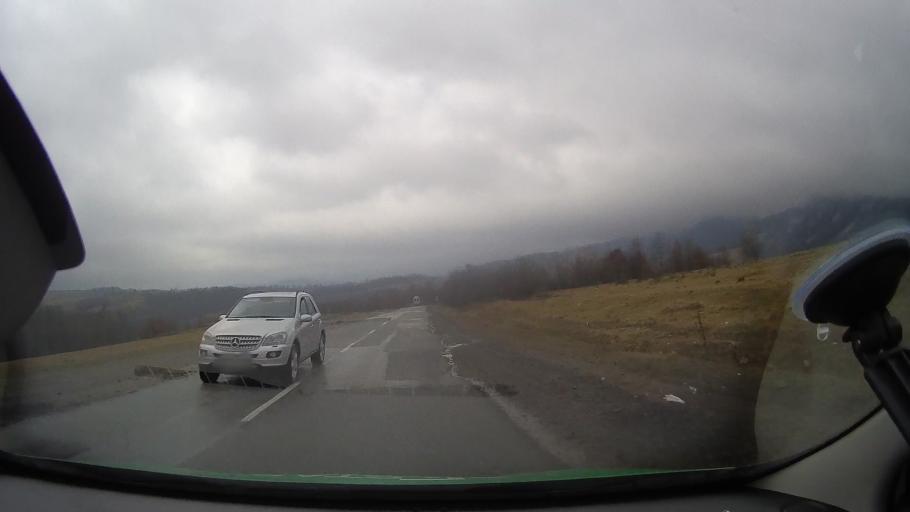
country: RO
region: Arad
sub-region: Comuna Varfurile
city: Varfurile
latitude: 46.2943
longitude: 22.5412
